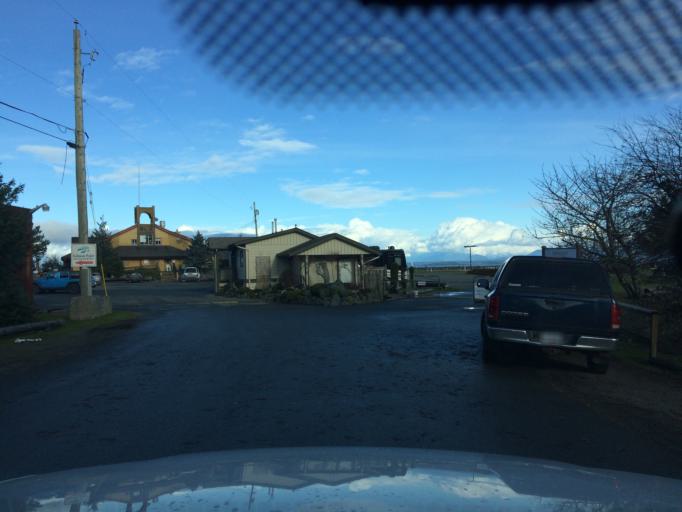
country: CA
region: British Columbia
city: Campbell River
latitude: 49.8886
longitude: -125.1259
